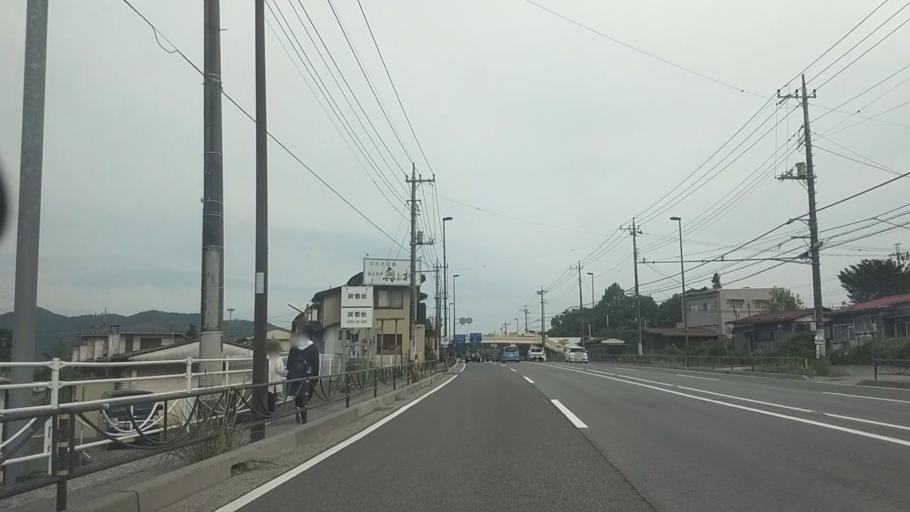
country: JP
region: Yamanashi
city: Fujikawaguchiko
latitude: 35.4778
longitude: 138.7874
